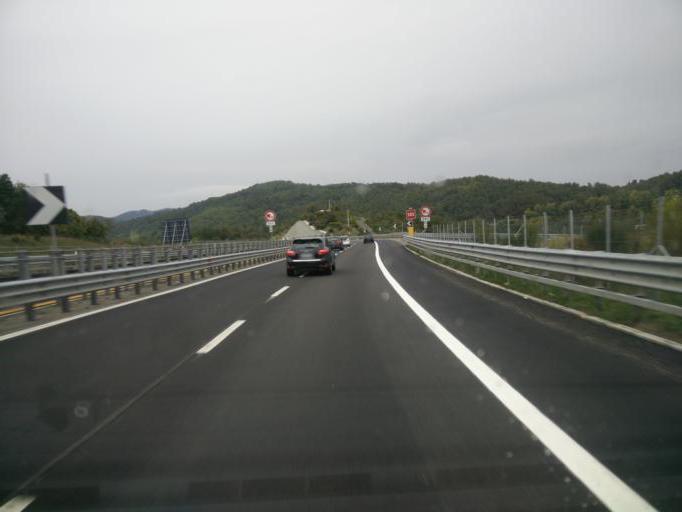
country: IT
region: Tuscany
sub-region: Province of Florence
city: Barberino di Mugello
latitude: 44.0347
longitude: 11.2243
